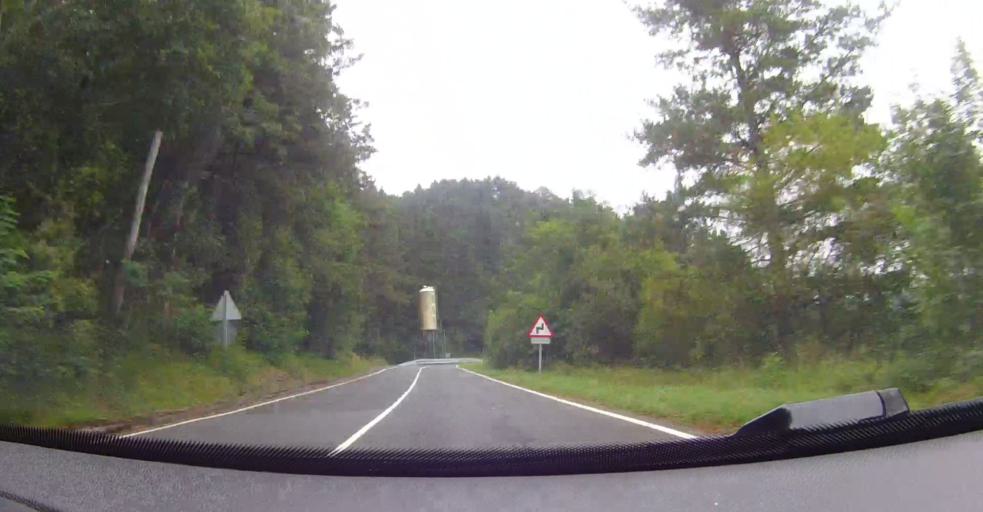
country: ES
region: Basque Country
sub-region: Bizkaia
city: Balmaseda
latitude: 43.2442
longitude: -3.3009
